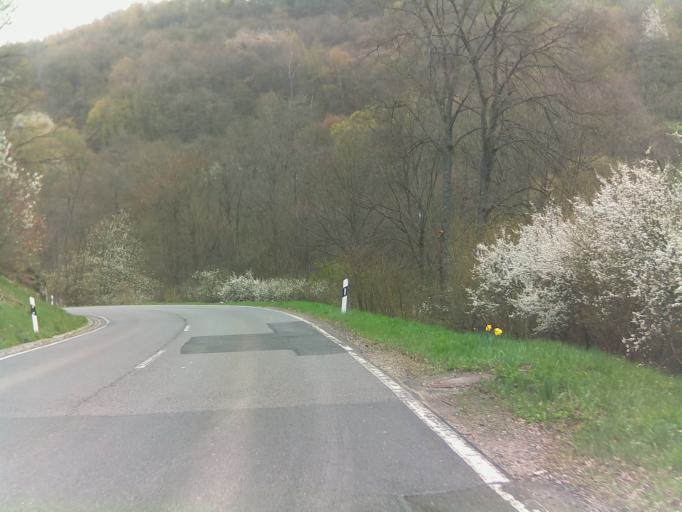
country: DE
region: Rheinland-Pfalz
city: Hennweiler
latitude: 49.8001
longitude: 7.4308
